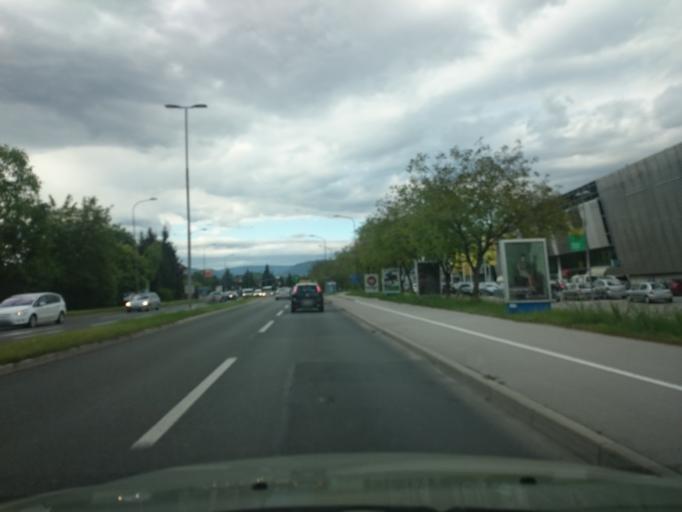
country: SI
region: Celje
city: Trnovlje pri Celju
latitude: 46.2488
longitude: 15.2801
